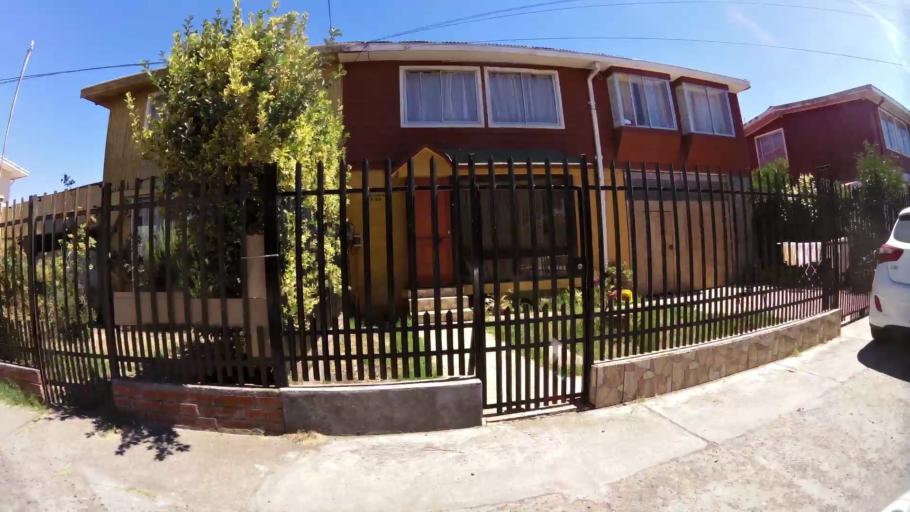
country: CL
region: Biobio
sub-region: Provincia de Concepcion
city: Talcahuano
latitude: -36.7596
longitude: -73.0914
